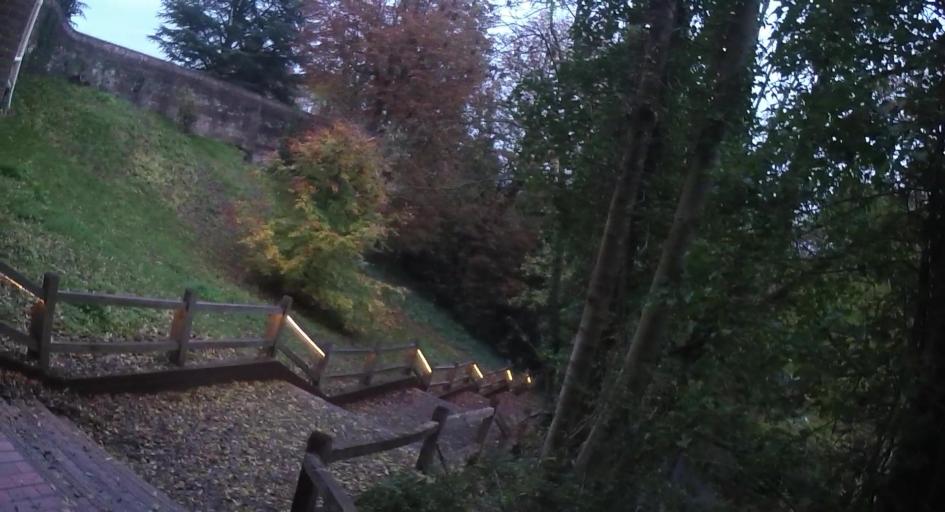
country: GB
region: England
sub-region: Surrey
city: Farnham
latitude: 51.2181
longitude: -0.8031
